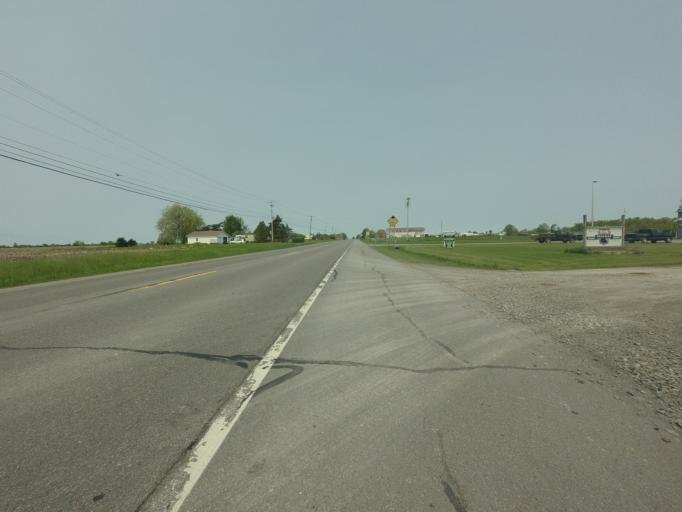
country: US
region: New York
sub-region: Jefferson County
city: Dexter
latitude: 44.0576
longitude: -76.1129
